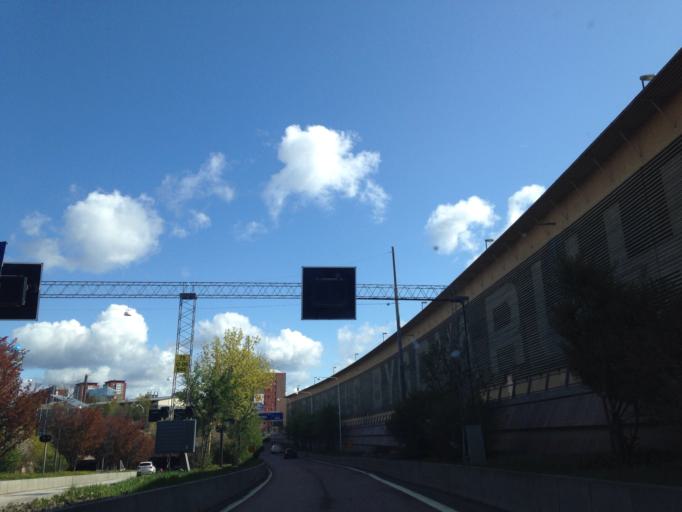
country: SE
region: Stockholm
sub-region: Stockholms Kommun
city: OEstermalm
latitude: 59.3027
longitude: 18.1126
